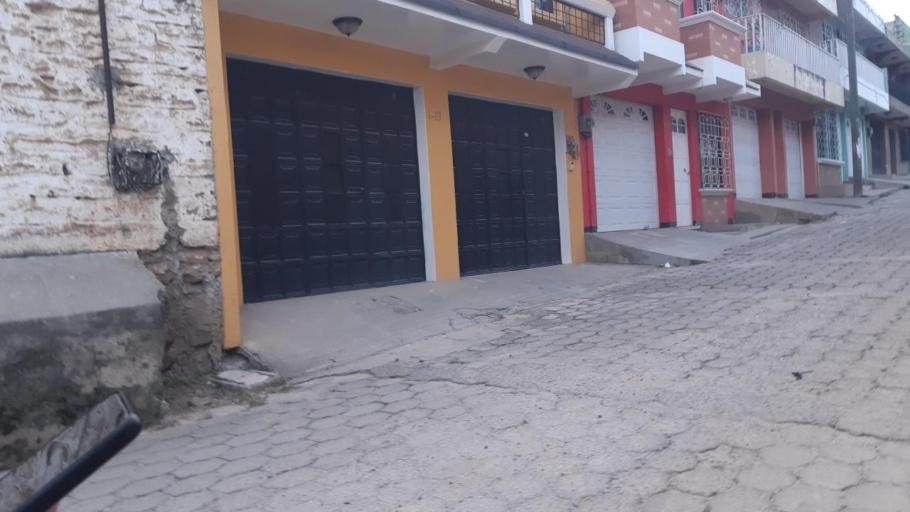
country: GT
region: Quetzaltenango
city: Salcaja
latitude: 14.8829
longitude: -91.4608
